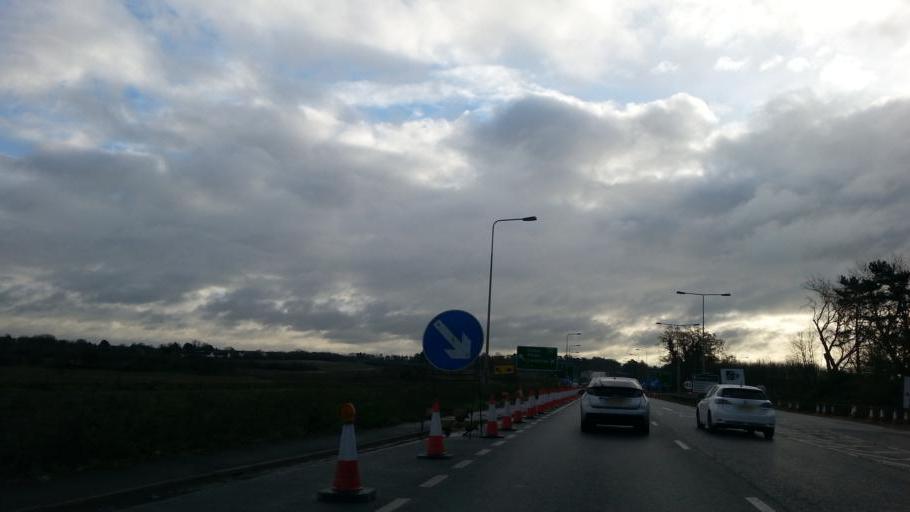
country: GB
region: England
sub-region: Cambridgeshire
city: Girton
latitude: 52.2352
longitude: 0.0684
